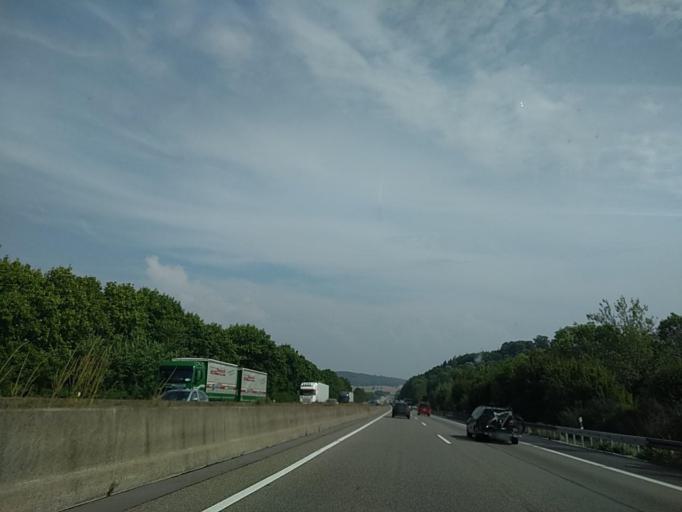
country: DE
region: North Rhine-Westphalia
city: Warburg
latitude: 51.4773
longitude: 9.0605
